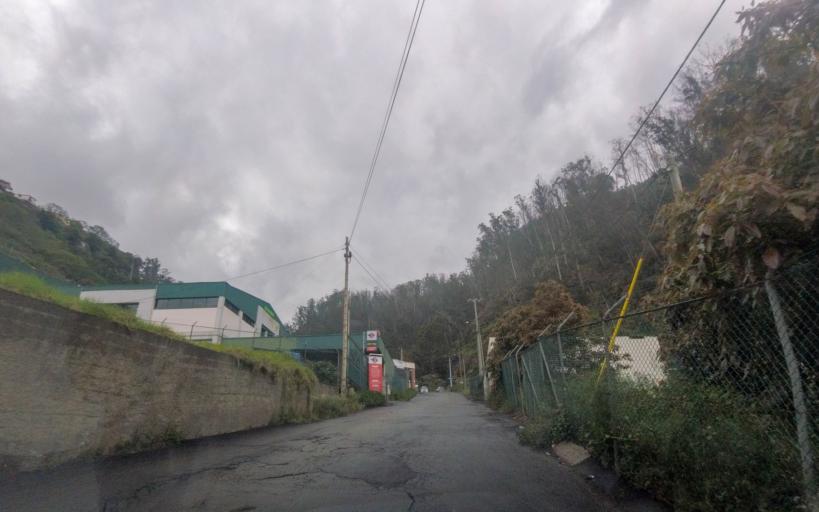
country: PT
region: Madeira
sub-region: Funchal
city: Nossa Senhora do Monte
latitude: 32.6774
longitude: -16.9351
